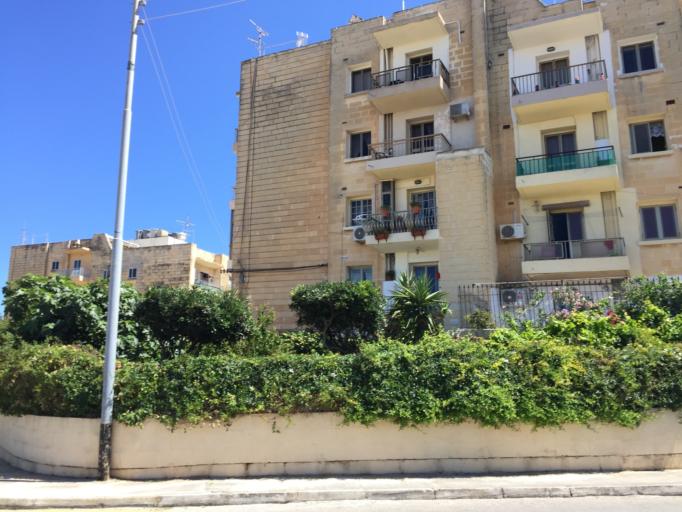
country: MT
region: Saint Julian
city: San Giljan
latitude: 35.9141
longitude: 14.4877
